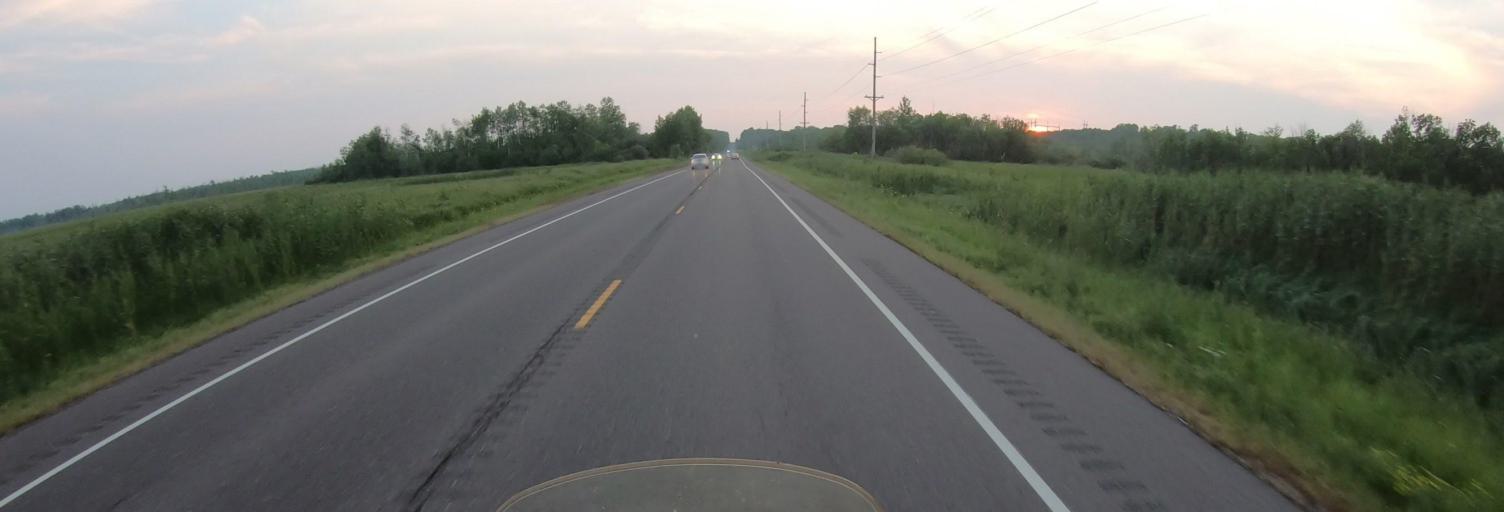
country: US
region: Minnesota
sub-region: Pine County
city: Rock Creek
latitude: 45.7735
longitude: -92.8320
